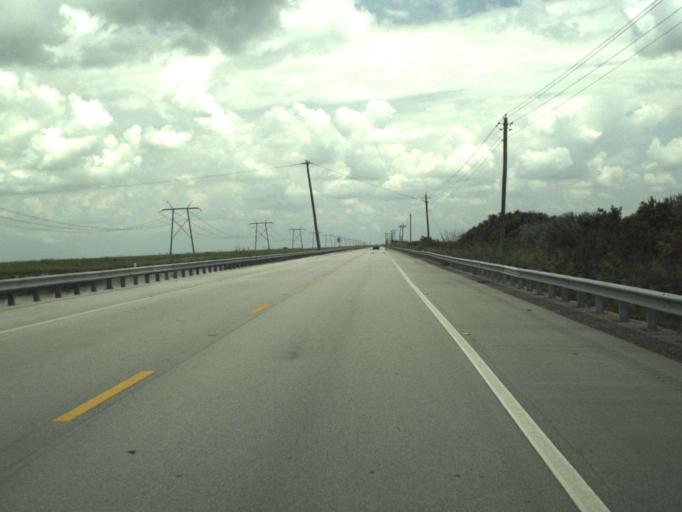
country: US
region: Florida
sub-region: Palm Beach County
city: Pahokee
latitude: 26.7562
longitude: -80.4886
